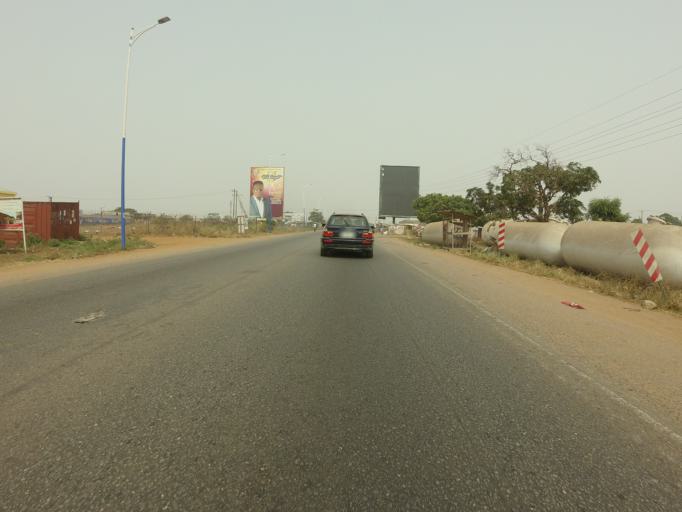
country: GH
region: Greater Accra
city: Tema
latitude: 5.7289
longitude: 0.0253
